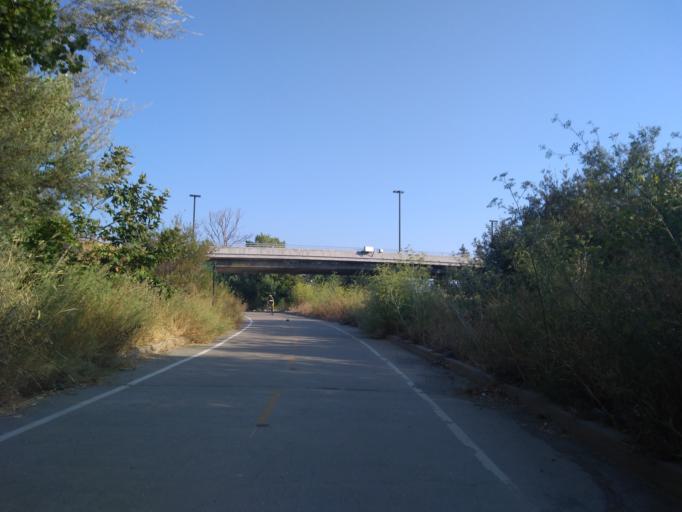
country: US
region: California
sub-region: Santa Clara County
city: Santa Clara
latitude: 37.3741
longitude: -121.9328
